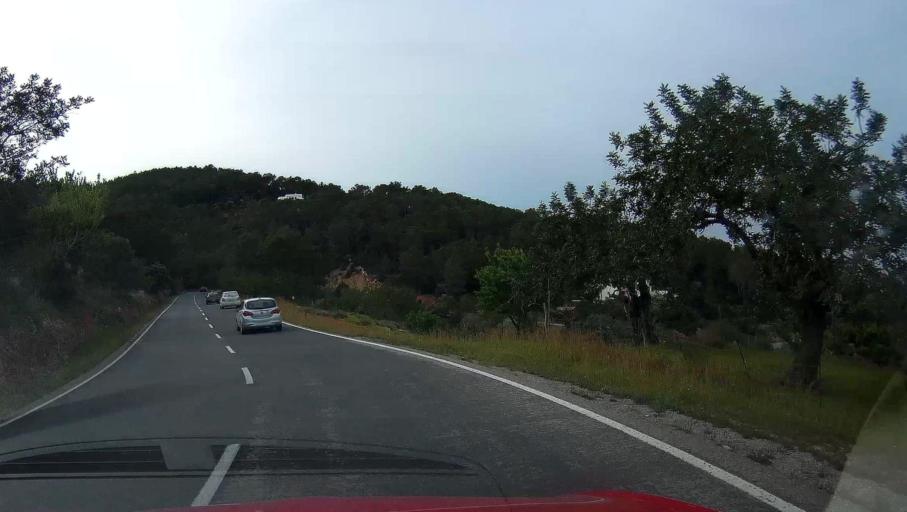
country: ES
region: Balearic Islands
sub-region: Illes Balears
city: Sant Joan de Labritja
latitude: 39.0820
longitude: 1.4973
